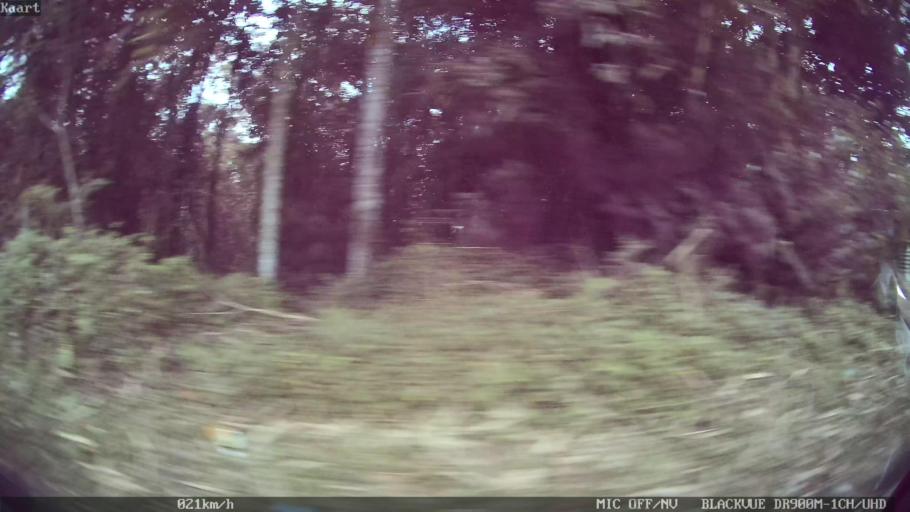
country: ID
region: Bali
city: Banjar Geriana Kangin
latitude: -8.4011
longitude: 115.4402
